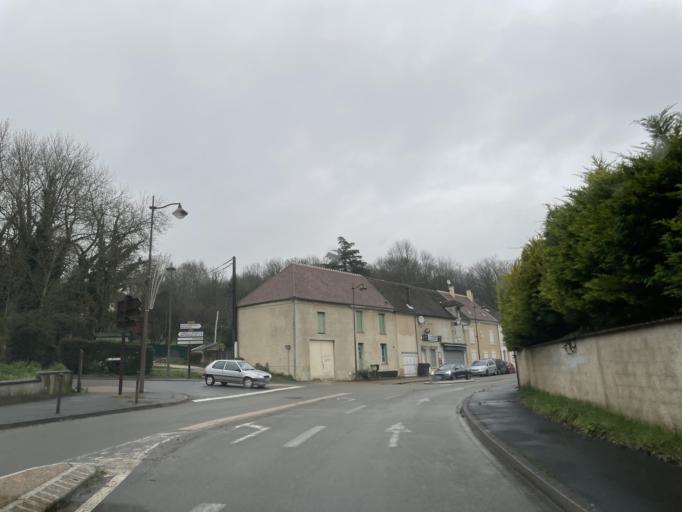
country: FR
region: Ile-de-France
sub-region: Departement de Seine-et-Marne
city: Pommeuse
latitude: 48.8186
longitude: 3.0135
